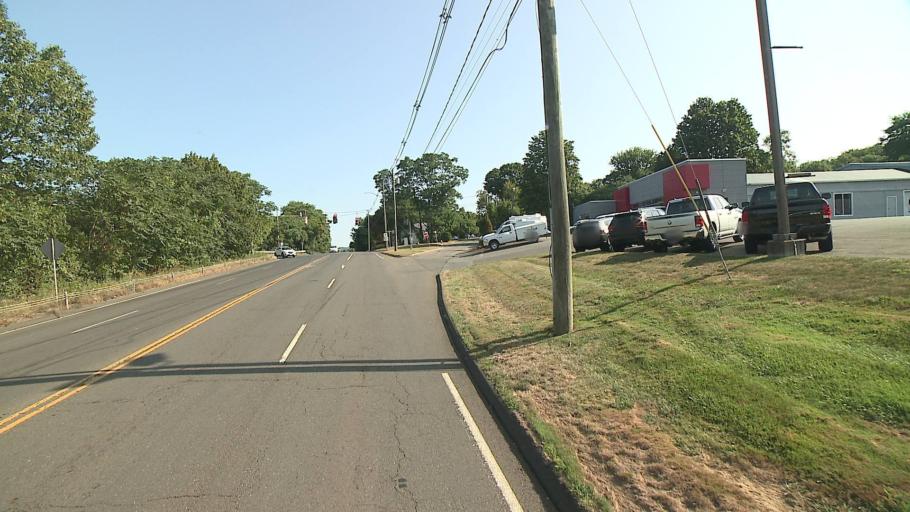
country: US
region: Connecticut
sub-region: New Haven County
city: Wallingford Center
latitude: 41.4446
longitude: -72.8301
